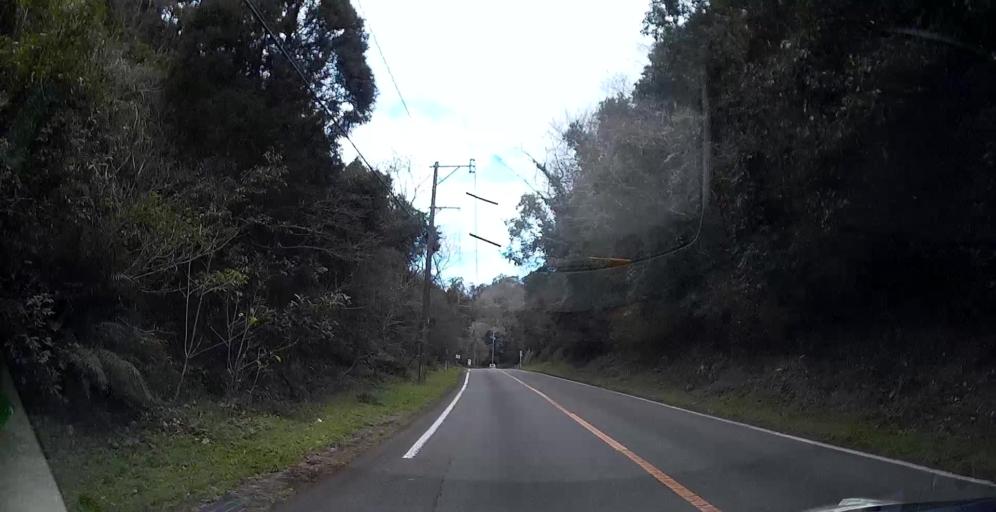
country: JP
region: Kumamoto
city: Yatsushiro
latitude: 32.3713
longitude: 130.5047
